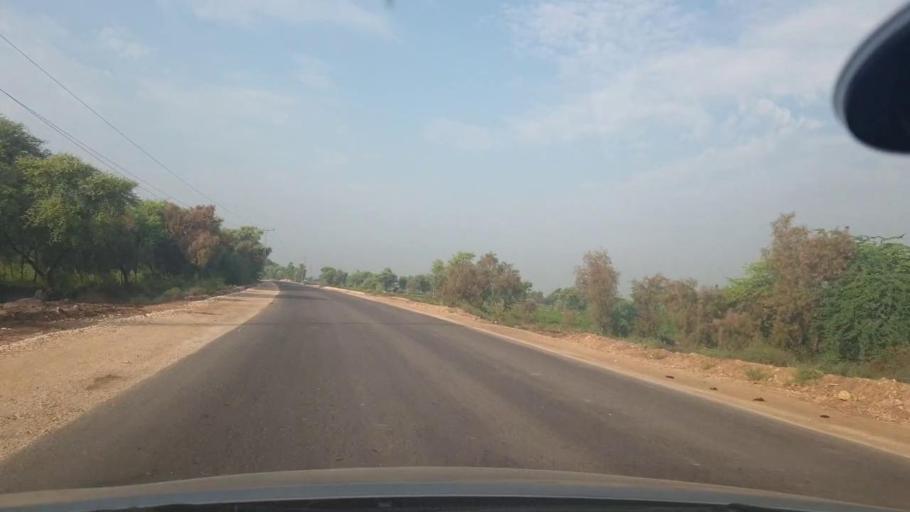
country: PK
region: Sindh
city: Jacobabad
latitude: 28.2438
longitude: 68.3954
